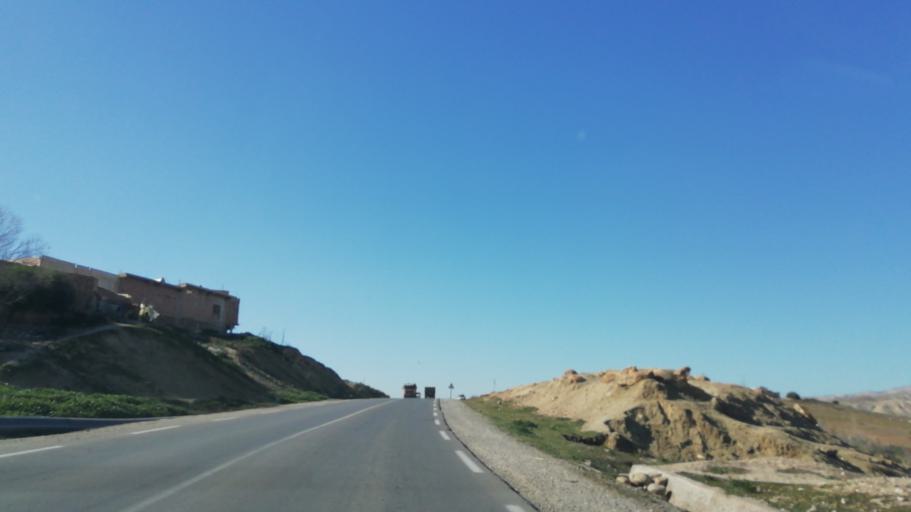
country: DZ
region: Mascara
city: Oued el Abtal
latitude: 35.4561
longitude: 0.7101
